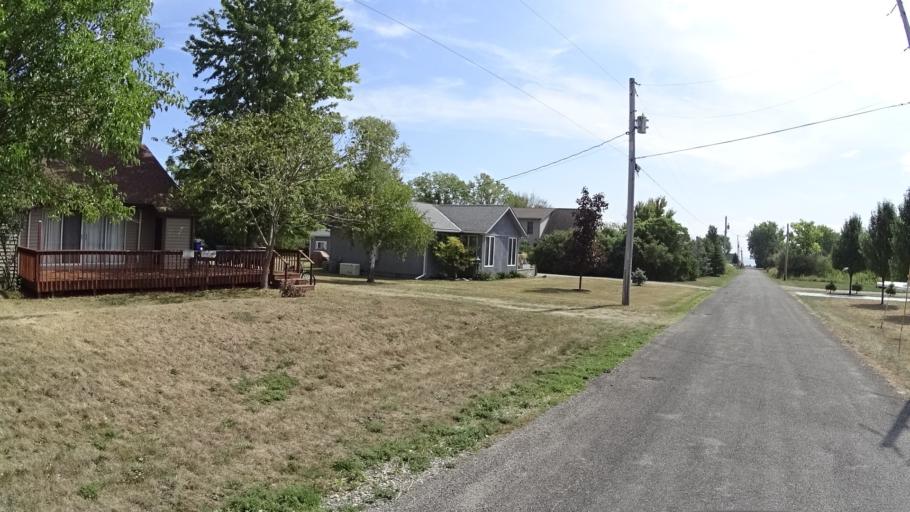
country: US
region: Ohio
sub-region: Erie County
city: Sandusky
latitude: 41.5900
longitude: -82.6910
